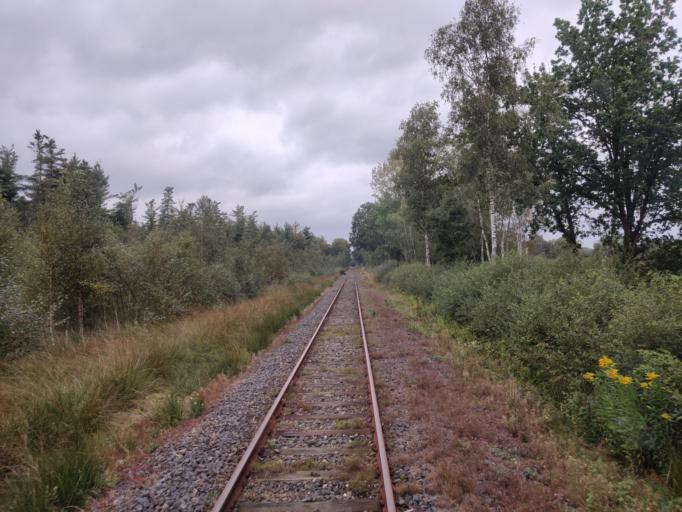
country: DE
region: Lower Saxony
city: Gnarrenburg
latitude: 53.4003
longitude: 9.0127
